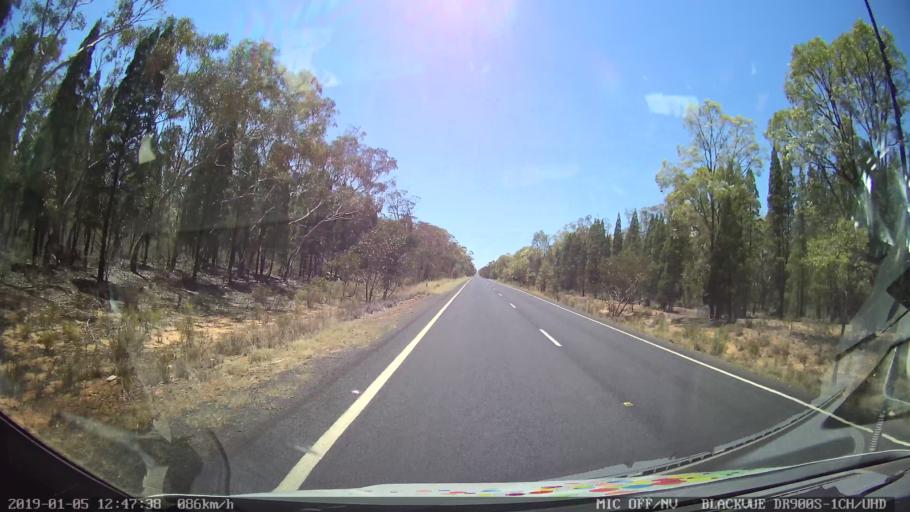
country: AU
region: New South Wales
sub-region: Warrumbungle Shire
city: Coonabarabran
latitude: -31.1183
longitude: 149.5794
